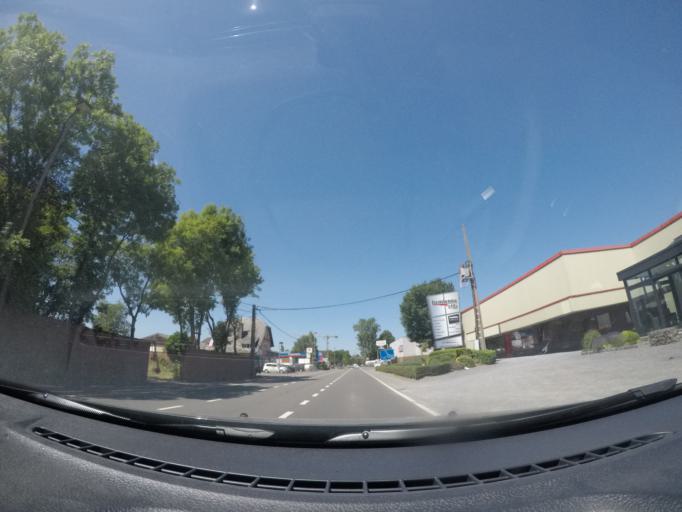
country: BE
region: Wallonia
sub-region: Province de Namur
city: Beauraing
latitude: 50.1181
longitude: 4.9553
